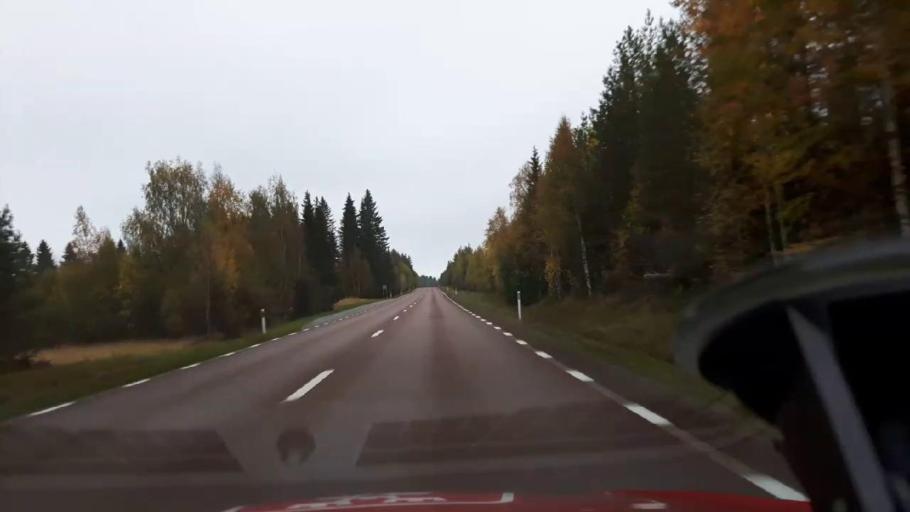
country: SE
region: Jaemtland
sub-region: Bergs Kommun
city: Hoverberg
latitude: 62.5836
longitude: 14.4400
